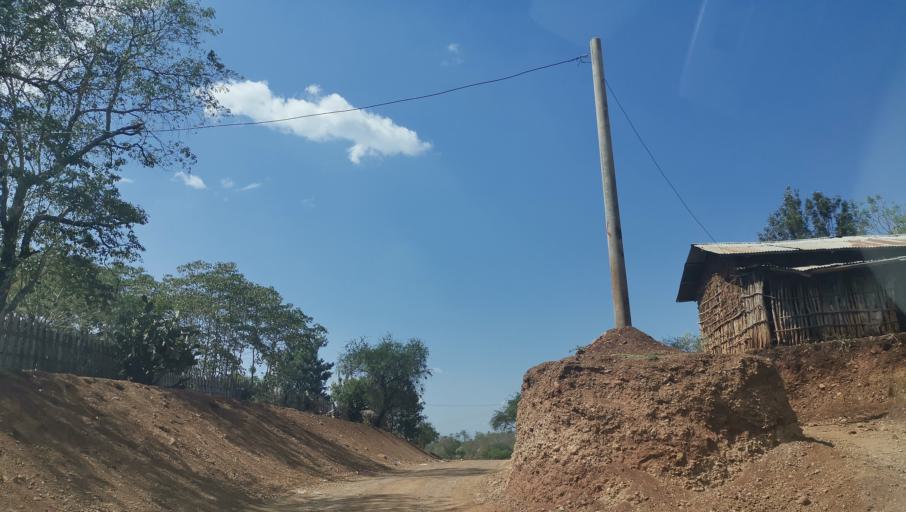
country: ET
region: Southern Nations, Nationalities, and People's Region
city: Arba Minch'
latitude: 6.3388
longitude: 37.2910
